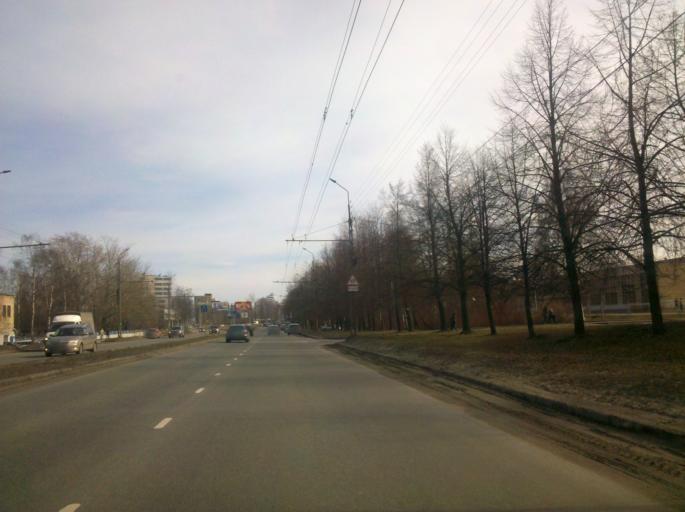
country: RU
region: Republic of Karelia
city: Petrozavodsk
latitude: 61.8021
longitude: 34.3533
